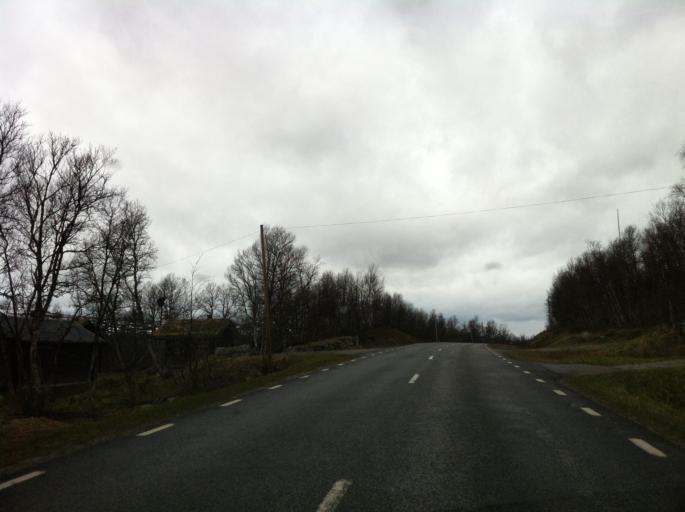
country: NO
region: Sor-Trondelag
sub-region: Tydal
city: Aas
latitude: 62.6005
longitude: 12.1760
